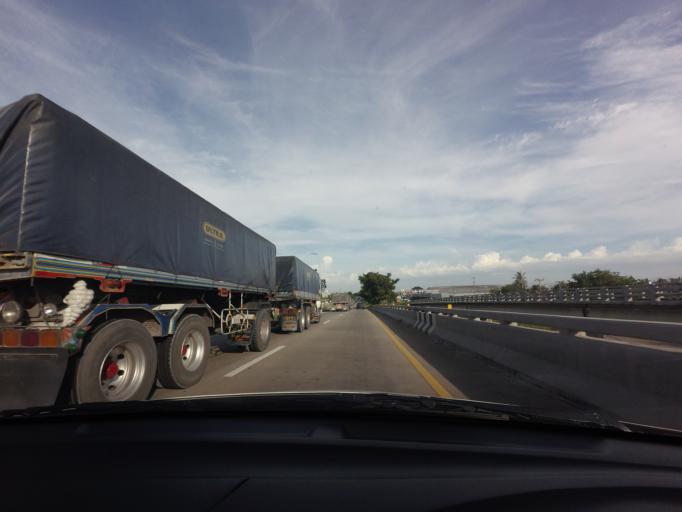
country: TH
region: Pathum Thani
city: Lat Lum Kaeo
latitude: 14.0572
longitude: 100.3321
